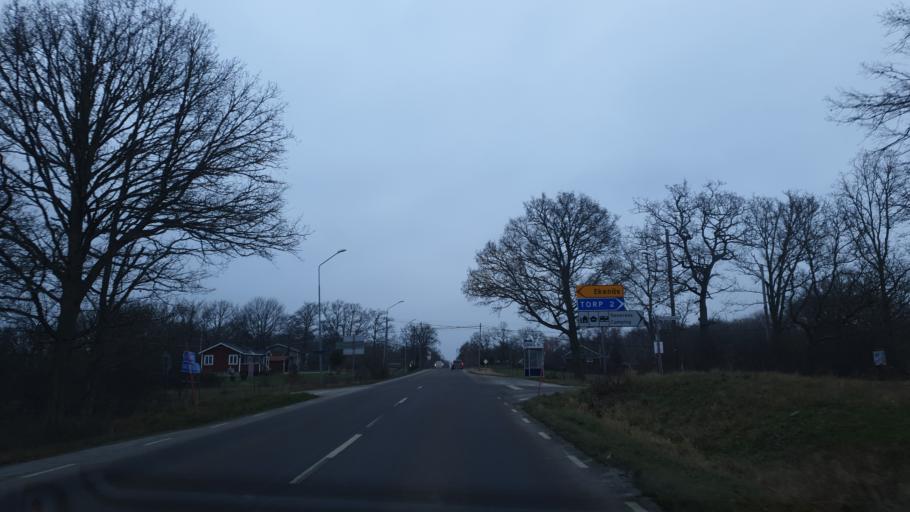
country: SE
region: Blekinge
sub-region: Karlskrona Kommun
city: Sturko
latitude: 56.1234
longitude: 15.7358
